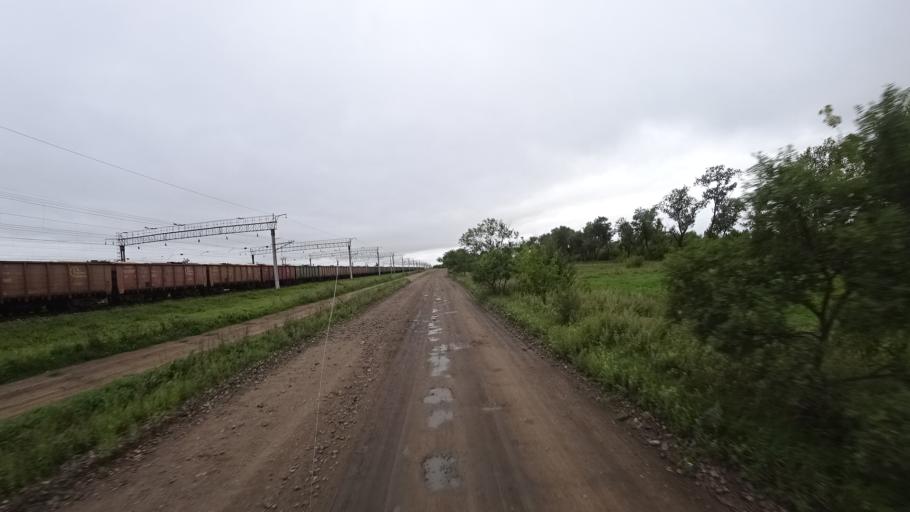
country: RU
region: Primorskiy
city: Chernigovka
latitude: 44.3412
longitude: 132.5344
